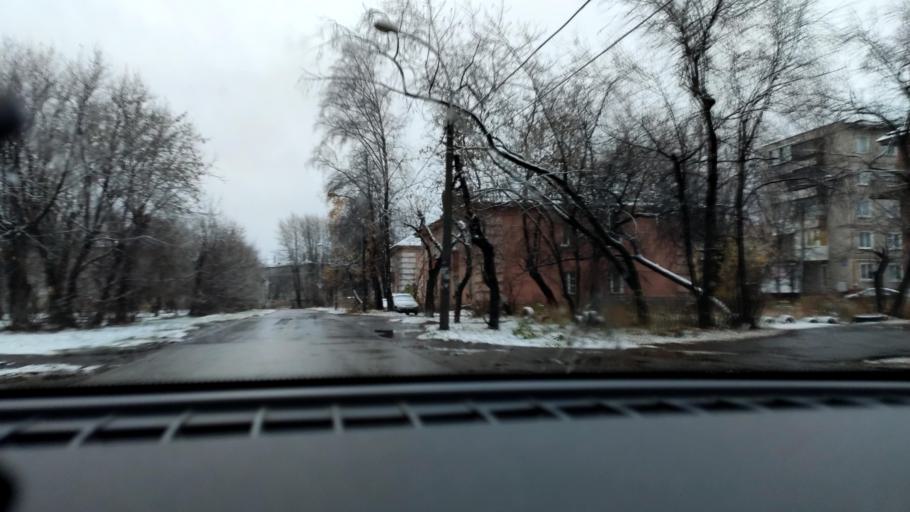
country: RU
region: Perm
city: Kultayevo
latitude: 57.9969
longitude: 55.9419
